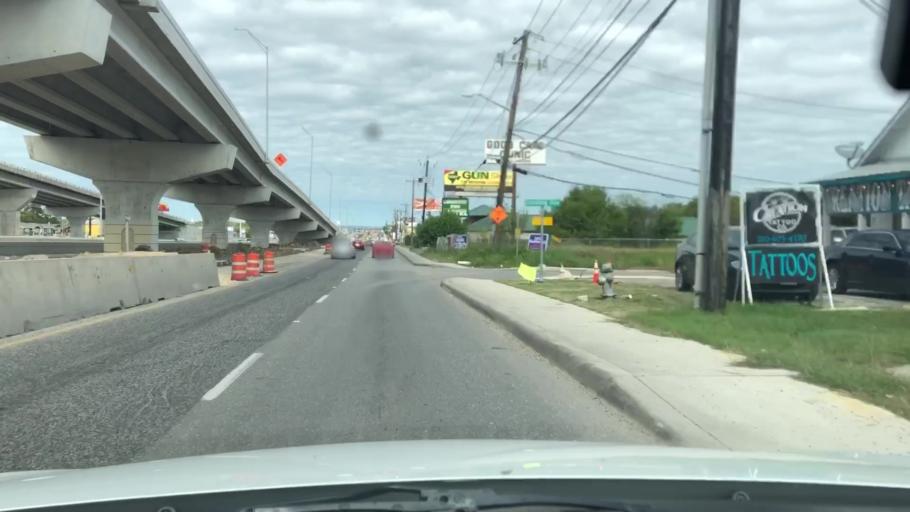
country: US
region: Texas
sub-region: Bexar County
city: Lackland Air Force Base
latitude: 29.4013
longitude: -98.6493
